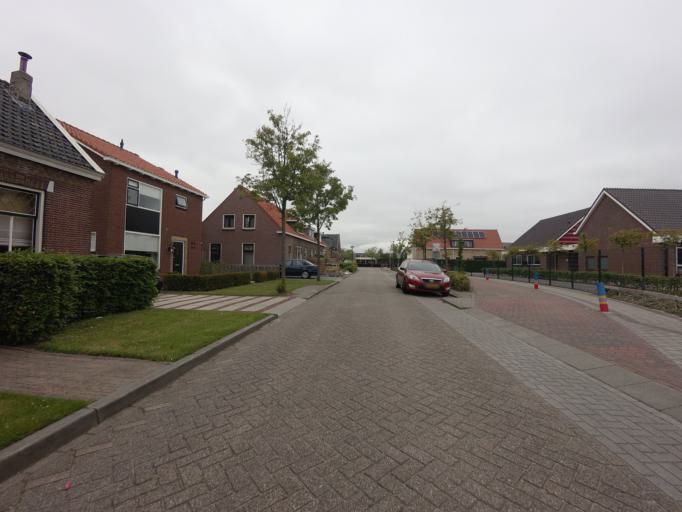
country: NL
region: South Holland
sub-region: Gemeente Spijkenisse
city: Spijkenisse
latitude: 51.8121
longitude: 4.3385
